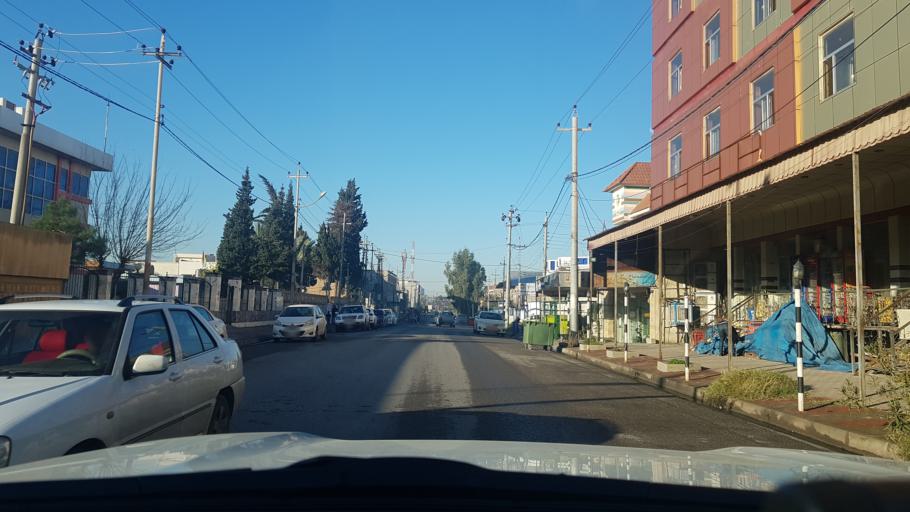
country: IQ
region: Arbil
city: Erbil
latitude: 36.2066
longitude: 44.0081
